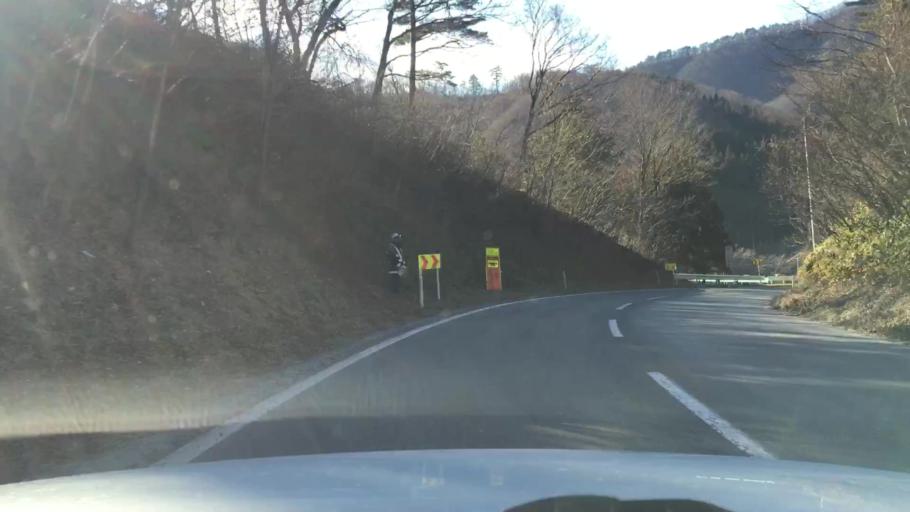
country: JP
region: Iwate
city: Miyako
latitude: 39.6158
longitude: 141.7984
